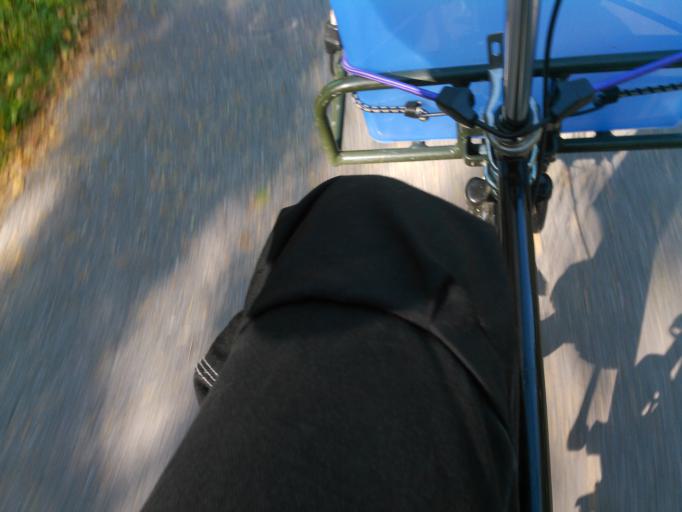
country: SE
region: Vaesterbotten
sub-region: Umea Kommun
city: Umea
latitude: 63.8046
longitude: 20.3104
